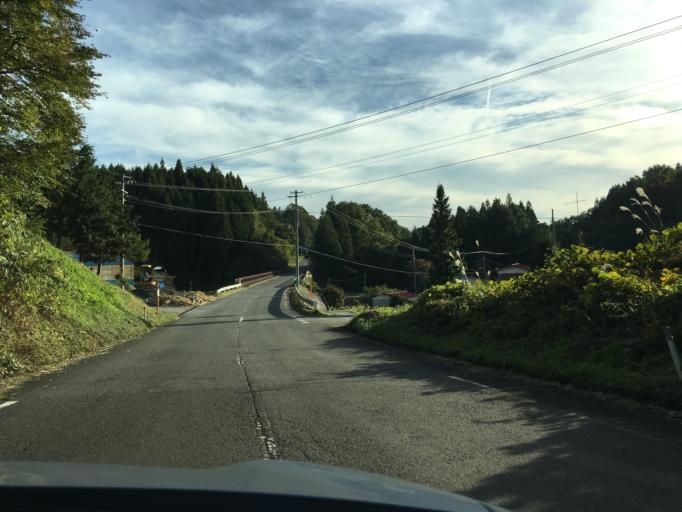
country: JP
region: Fukushima
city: Ishikawa
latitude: 37.1985
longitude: 140.5398
